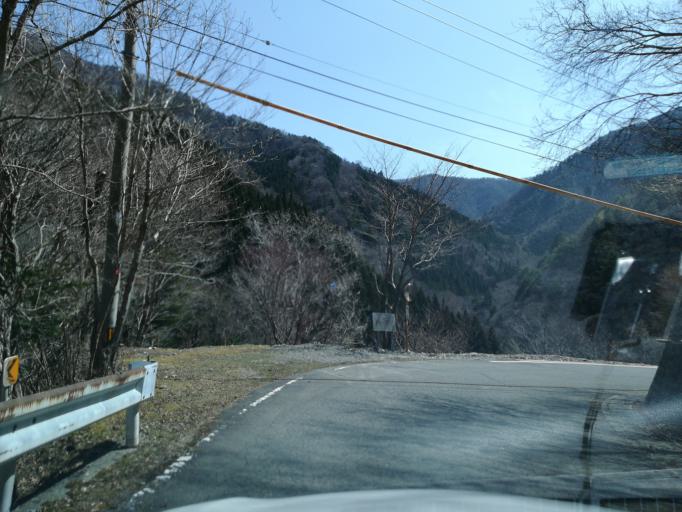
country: JP
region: Tokushima
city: Wakimachi
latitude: 33.8546
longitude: 134.0460
